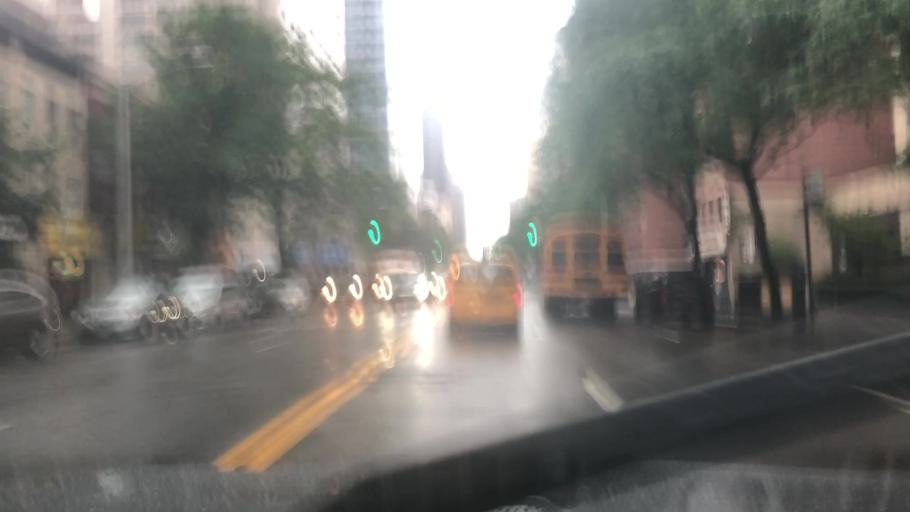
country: US
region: New York
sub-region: New York County
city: Manhattan
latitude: 40.7722
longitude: -73.9498
